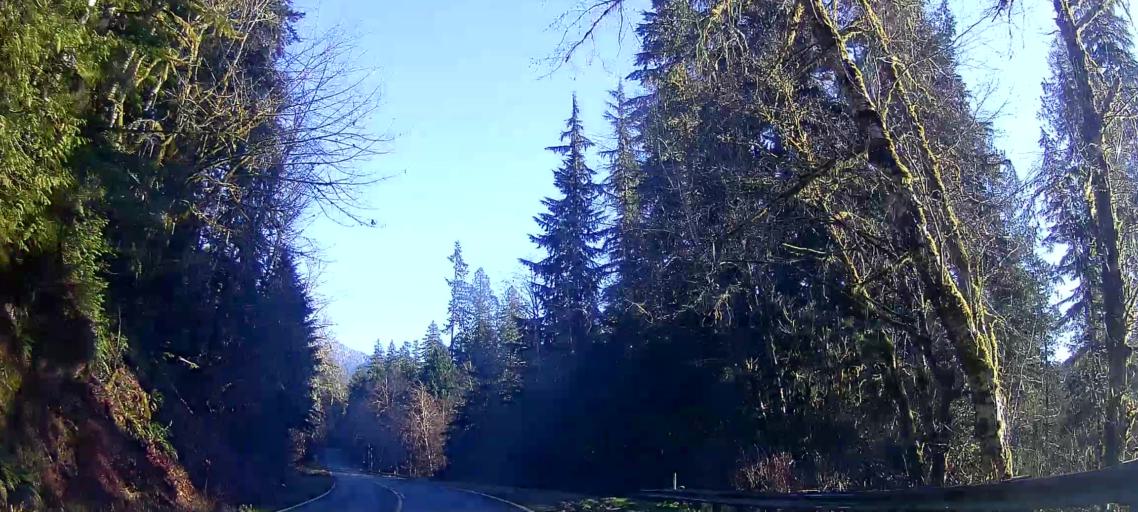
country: US
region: Washington
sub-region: Snohomish County
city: Darrington
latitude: 48.6487
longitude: -121.7260
